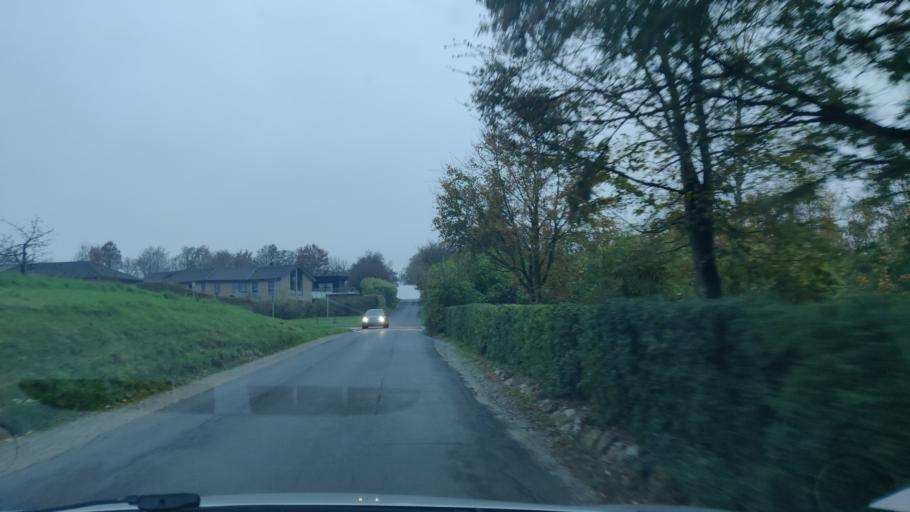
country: DK
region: South Denmark
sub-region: Kolding Kommune
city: Kolding
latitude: 55.5656
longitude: 9.4162
